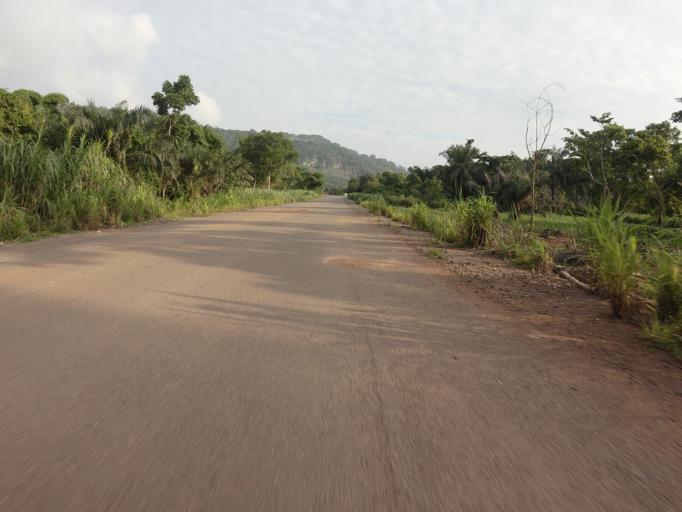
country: TG
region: Plateaux
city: Kpalime
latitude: 6.9252
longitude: 0.4616
